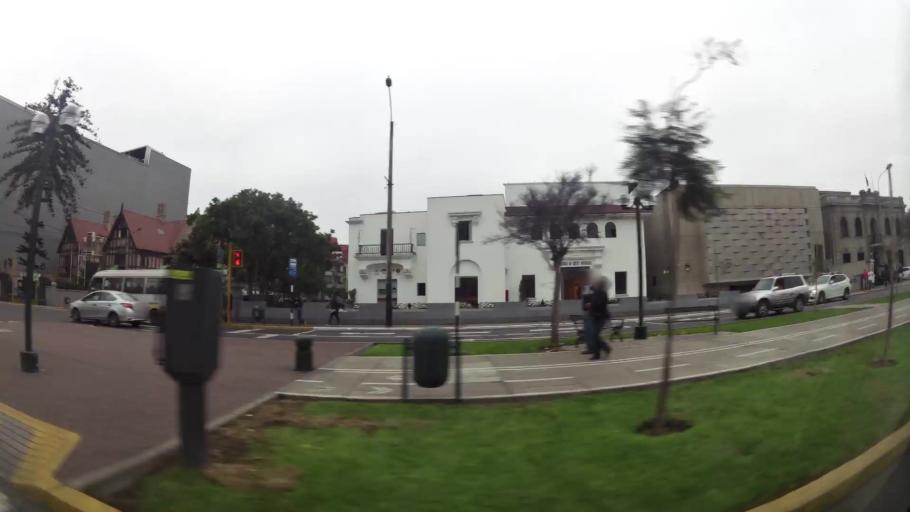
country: PE
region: Lima
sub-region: Lima
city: San Isidro
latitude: -12.1177
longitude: -77.0291
